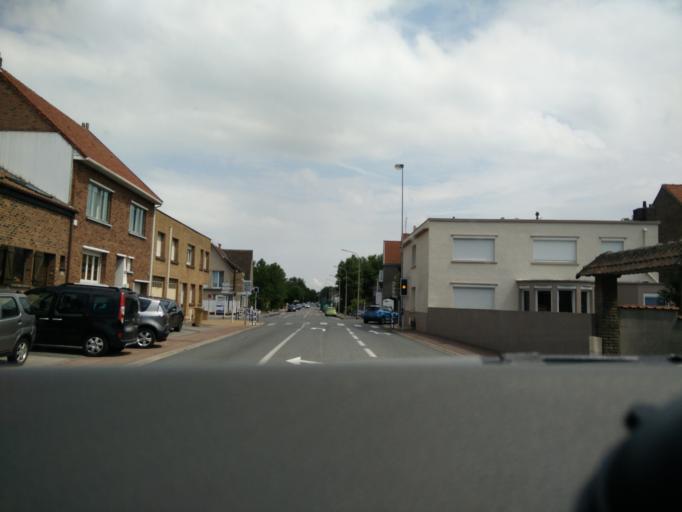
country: FR
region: Nord-Pas-de-Calais
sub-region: Departement du Nord
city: Bray-Dunes
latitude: 51.0754
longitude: 2.5135
